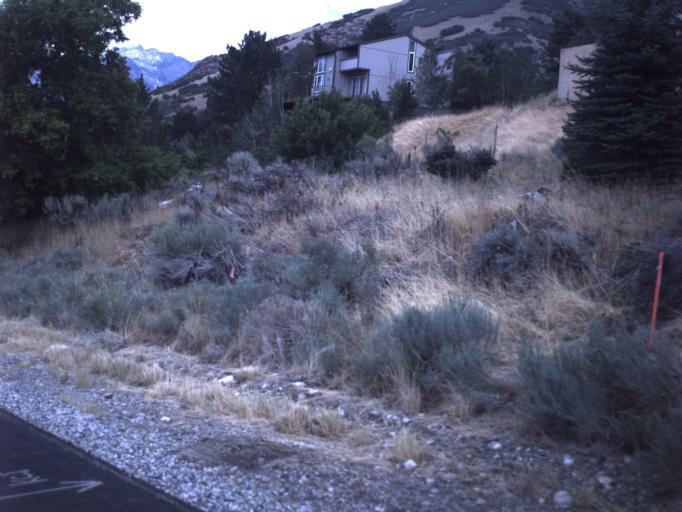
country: US
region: Utah
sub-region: Salt Lake County
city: Granite
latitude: 40.5865
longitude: -111.7922
